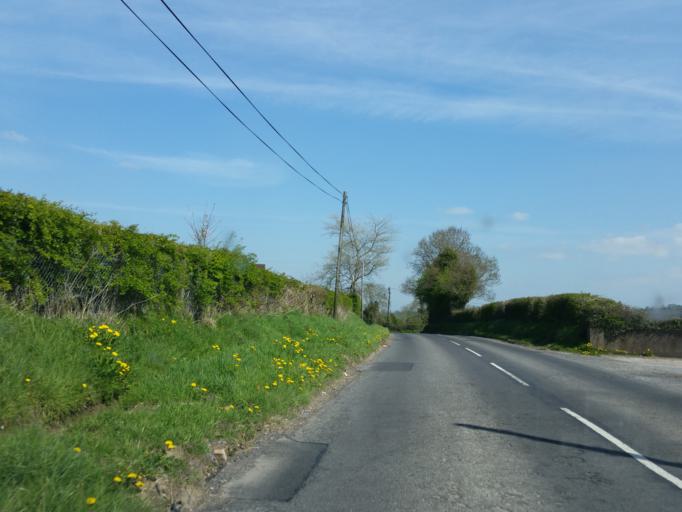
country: GB
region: Northern Ireland
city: Lisnaskea
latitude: 54.2949
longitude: -7.4200
